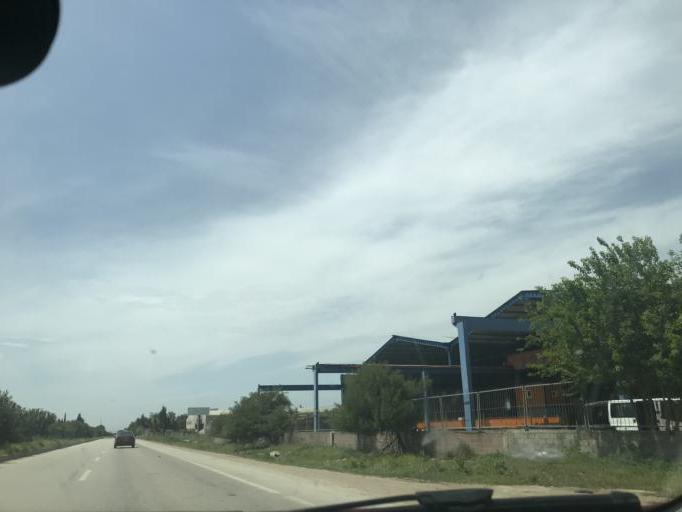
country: TR
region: Adana
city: Yakapinar
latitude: 36.9713
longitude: 35.5219
